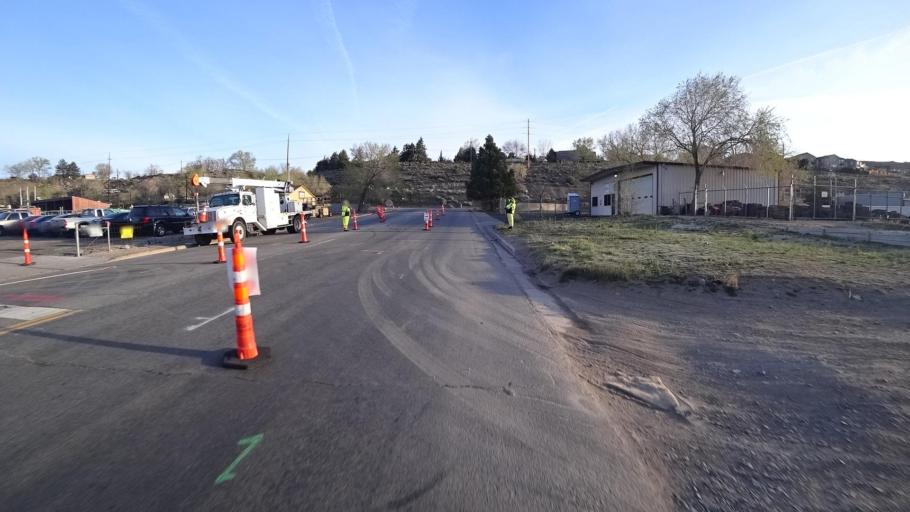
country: US
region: Nevada
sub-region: Washoe County
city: Mogul
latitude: 39.5086
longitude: -119.8966
